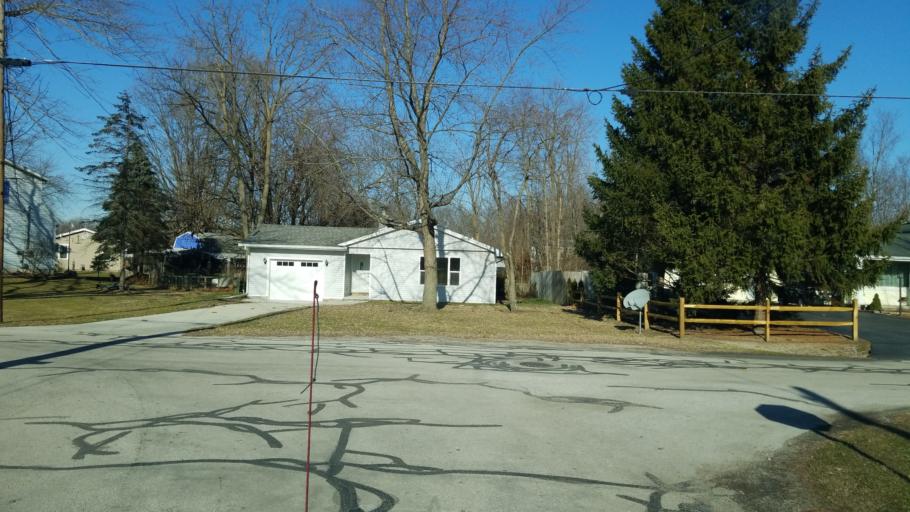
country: US
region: Ohio
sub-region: Wood County
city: Weston
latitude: 41.4112
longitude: -83.8585
